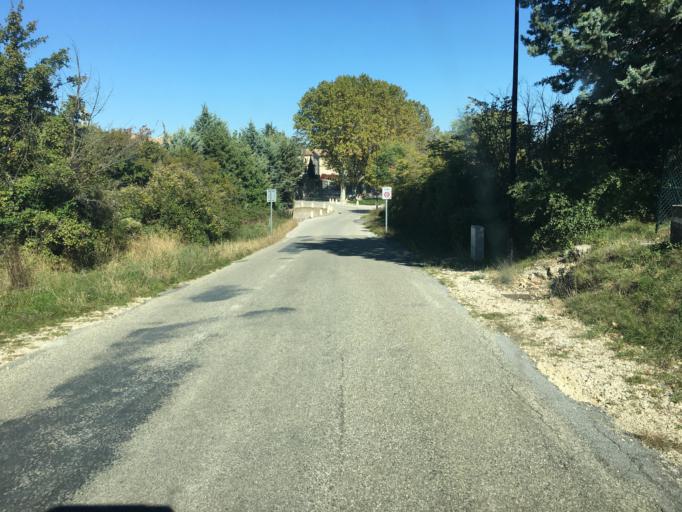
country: FR
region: Languedoc-Roussillon
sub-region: Departement du Gard
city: Barjac
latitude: 44.1837
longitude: 4.3289
